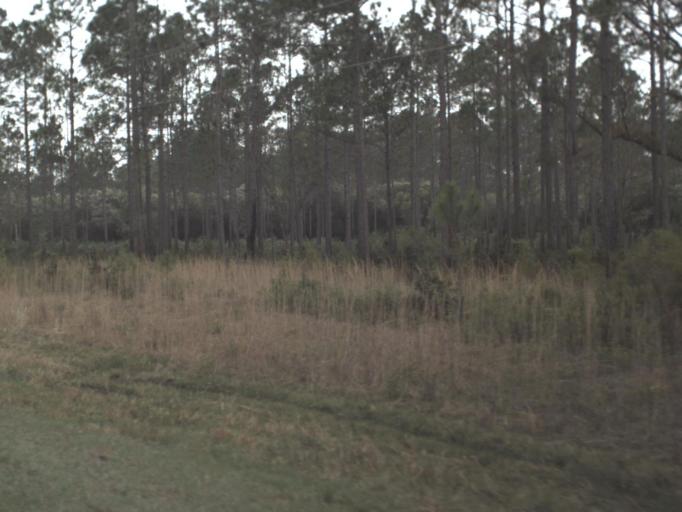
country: US
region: Florida
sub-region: Liberty County
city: Bristol
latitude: 30.2871
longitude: -84.8383
